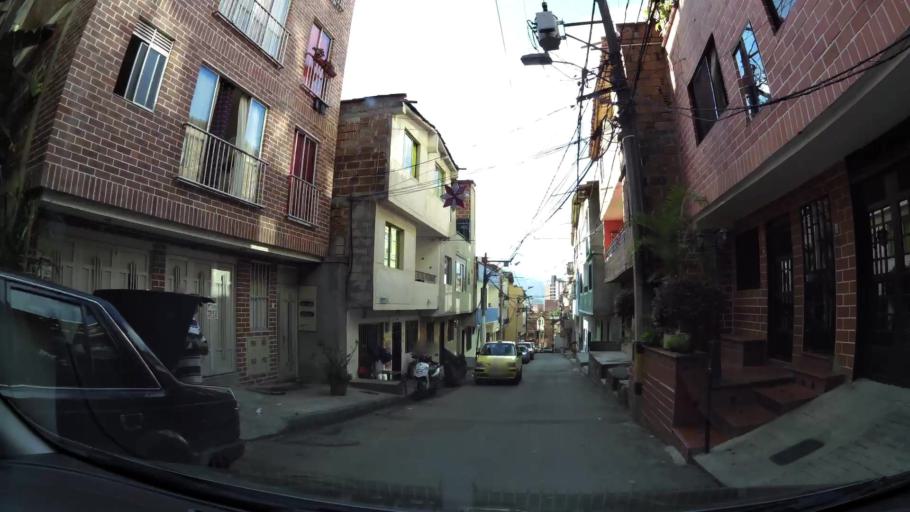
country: CO
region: Antioquia
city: Envigado
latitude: 6.1757
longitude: -75.5781
